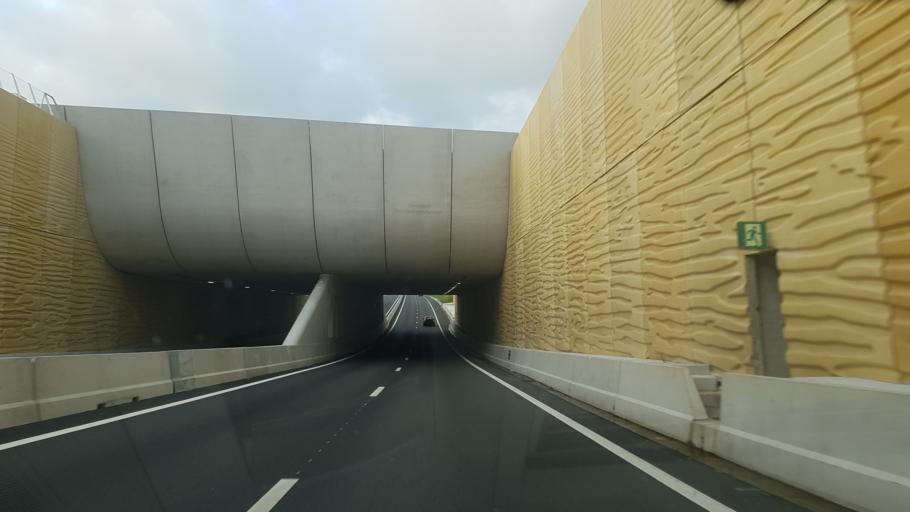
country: NL
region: Friesland
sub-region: Gemeente Harlingen
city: Harlingen
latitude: 53.1766
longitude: 5.4435
